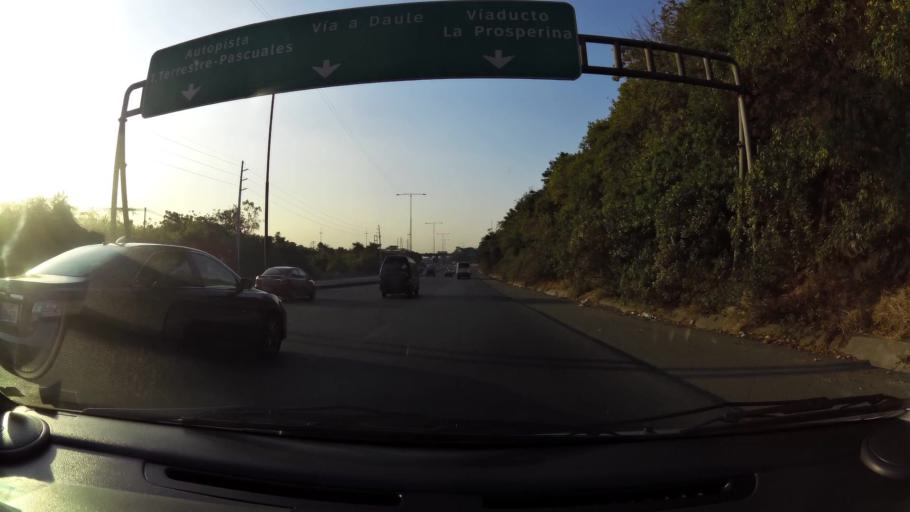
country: EC
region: Guayas
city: Santa Lucia
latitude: -2.1446
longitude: -79.9456
